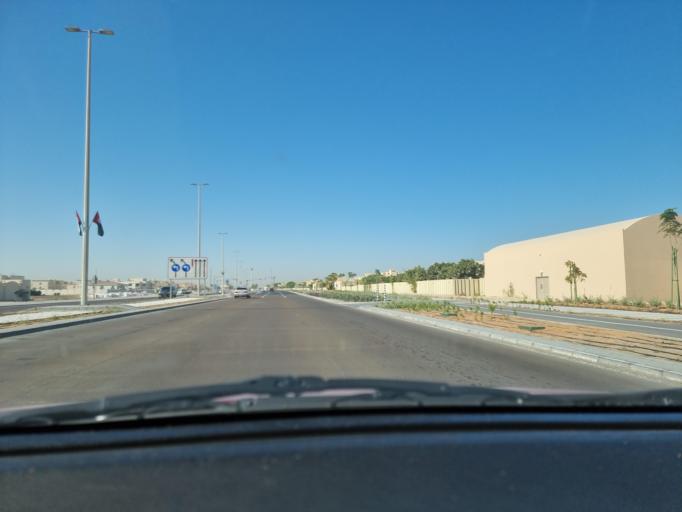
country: AE
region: Abu Dhabi
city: Abu Dhabi
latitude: 24.4388
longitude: 54.5932
